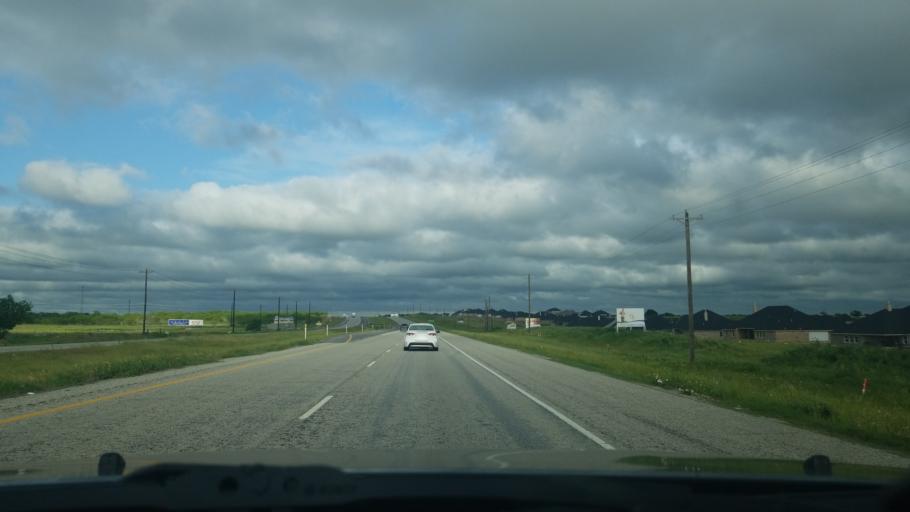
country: US
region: Texas
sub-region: Denton County
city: Ponder
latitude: 33.2420
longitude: -97.3661
